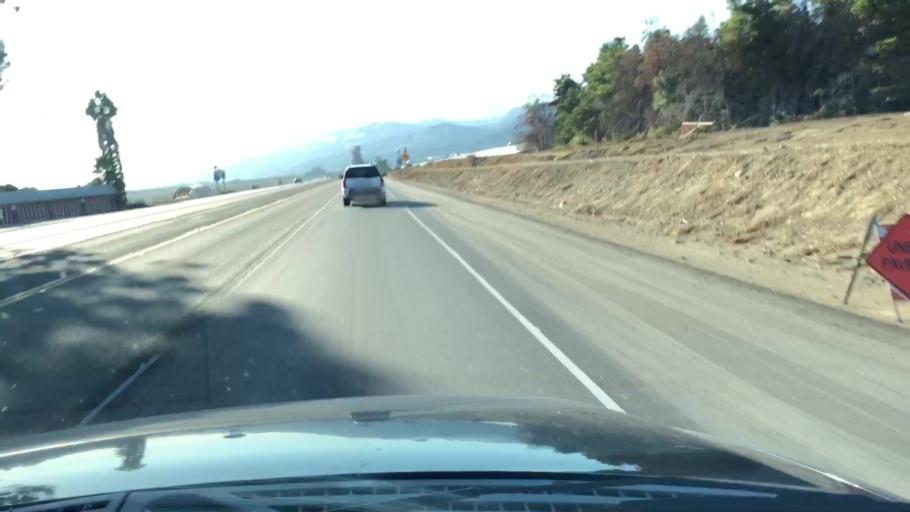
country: US
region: California
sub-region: Ventura County
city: Piru
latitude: 34.4069
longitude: -118.7562
